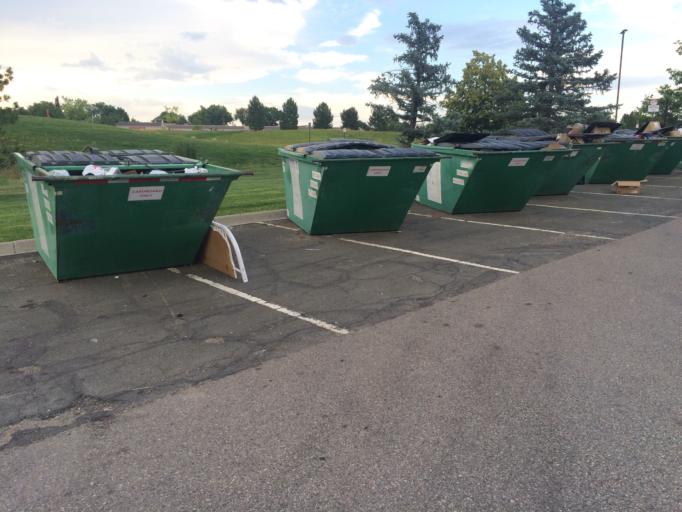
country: US
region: Colorado
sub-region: Adams County
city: Thornton
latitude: 39.8977
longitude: -104.9415
